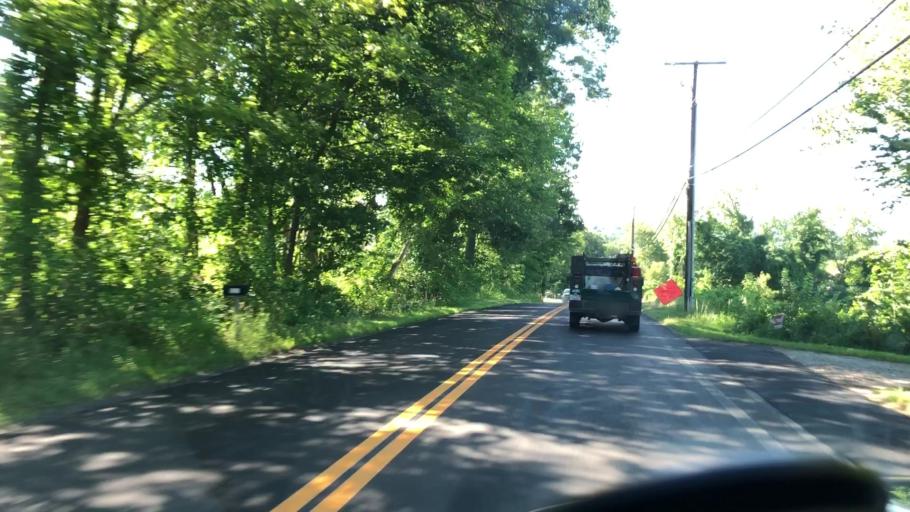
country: US
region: Massachusetts
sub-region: Hampshire County
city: Southampton
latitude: 42.2120
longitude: -72.7279
